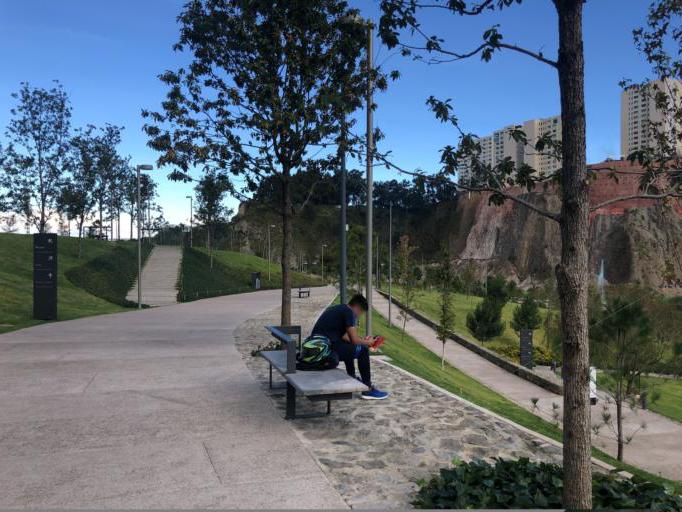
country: MX
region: Mexico City
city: Cuajimalpa
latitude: 19.3560
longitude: -99.2736
